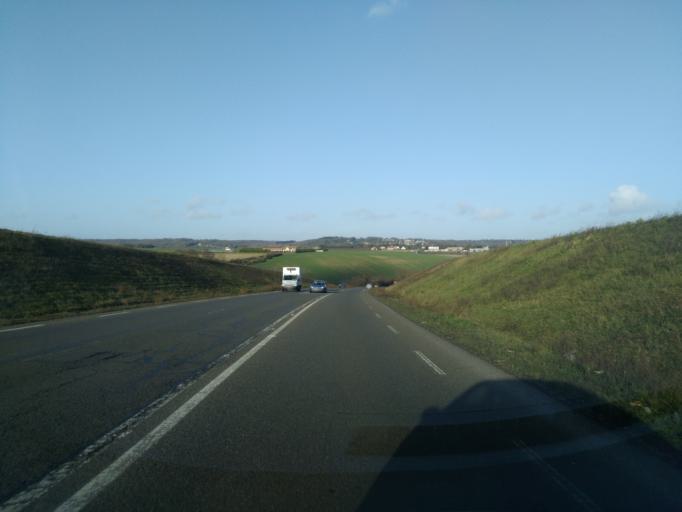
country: FR
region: Ile-de-France
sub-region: Departement des Yvelines
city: Feucherolles
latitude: 48.8485
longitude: 1.9613
